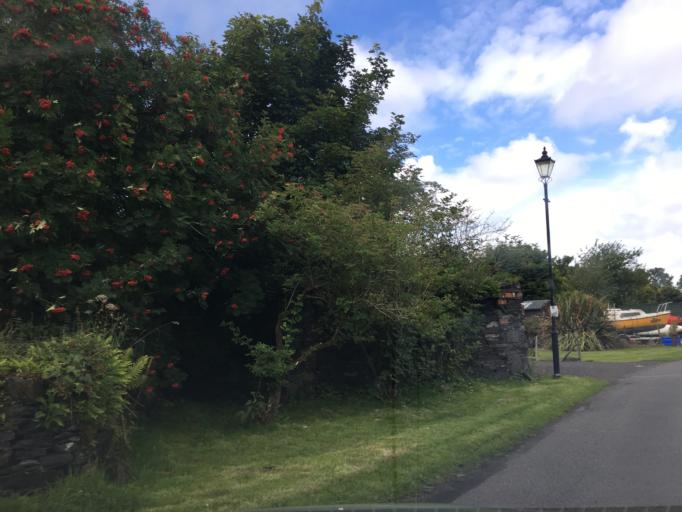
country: GB
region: Scotland
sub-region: Argyll and Bute
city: Oban
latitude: 56.2166
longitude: -5.6308
